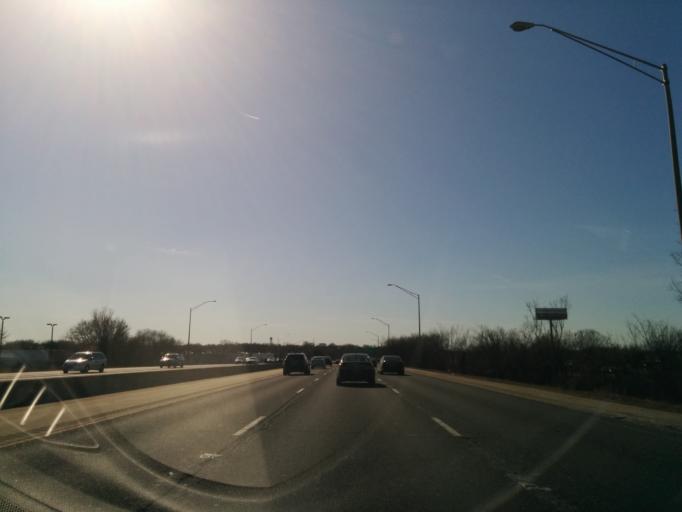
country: US
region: Illinois
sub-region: DuPage County
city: Burr Ridge
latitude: 41.7468
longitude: -87.9362
